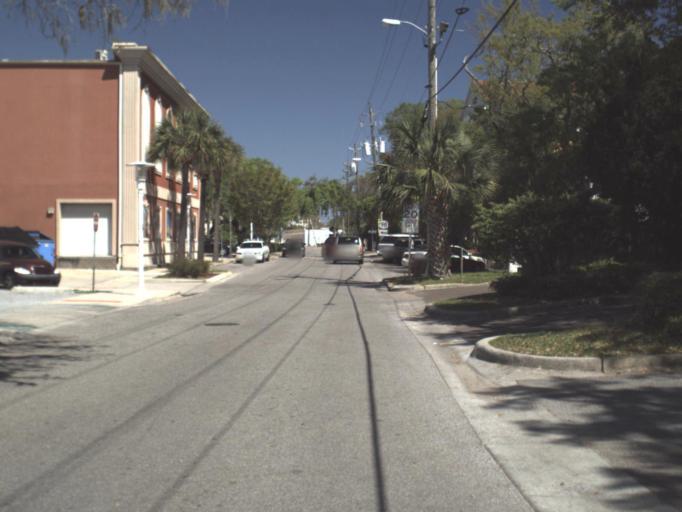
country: US
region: Florida
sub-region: Okaloosa County
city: Fort Walton Beach
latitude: 30.4029
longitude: -86.6051
